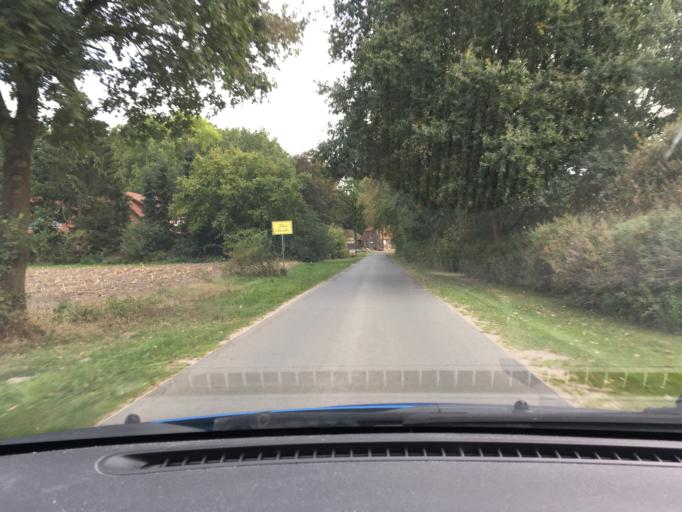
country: DE
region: Lower Saxony
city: Wietzendorf
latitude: 52.9018
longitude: 9.9588
